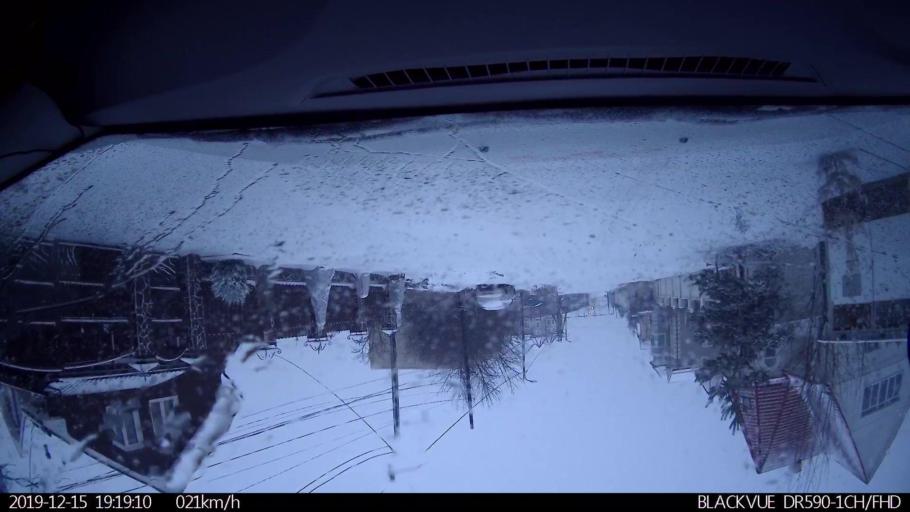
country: RU
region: Nizjnij Novgorod
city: Afonino
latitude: 56.3031
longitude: 44.0891
